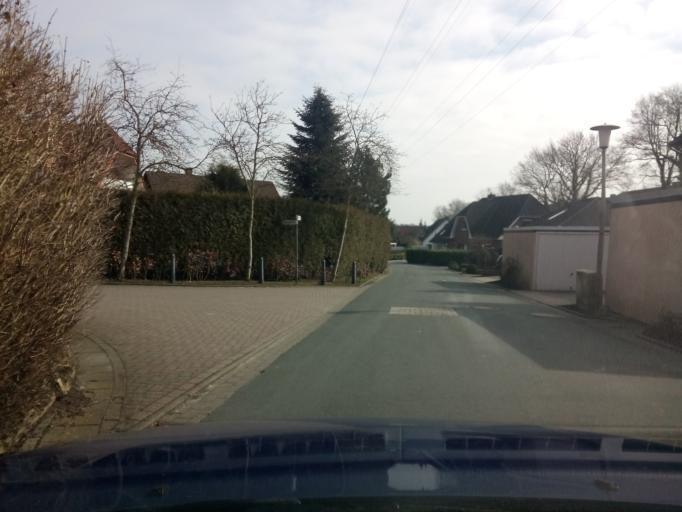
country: DE
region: Lower Saxony
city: Osterholz-Scharmbeck
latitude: 53.2242
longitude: 8.7791
